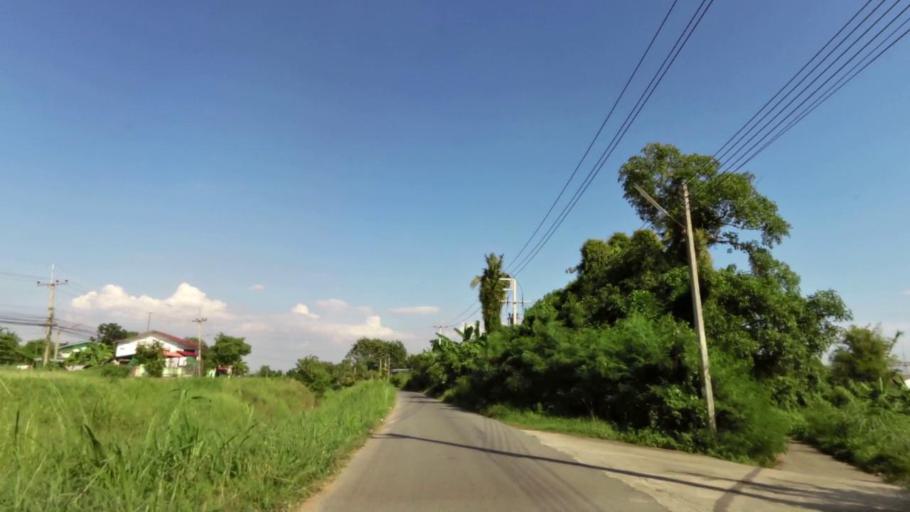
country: TH
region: Ang Thong
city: Ang Thong
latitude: 14.5855
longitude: 100.4632
